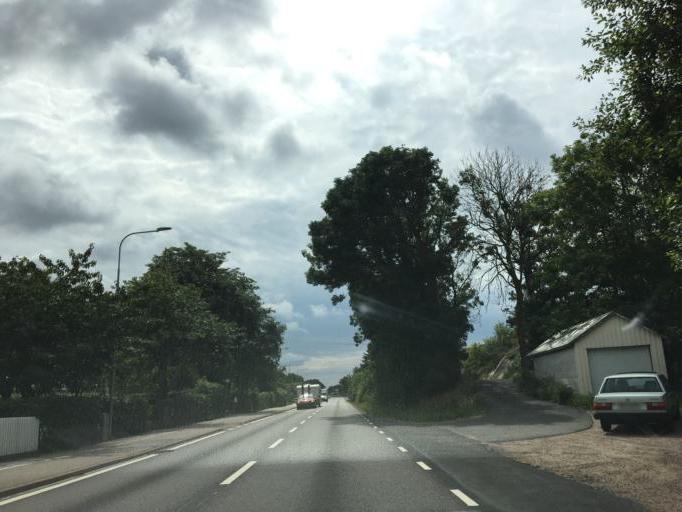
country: SE
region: Vaestra Goetaland
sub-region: Sotenas Kommun
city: Kungshamn
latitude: 58.3712
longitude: 11.2512
